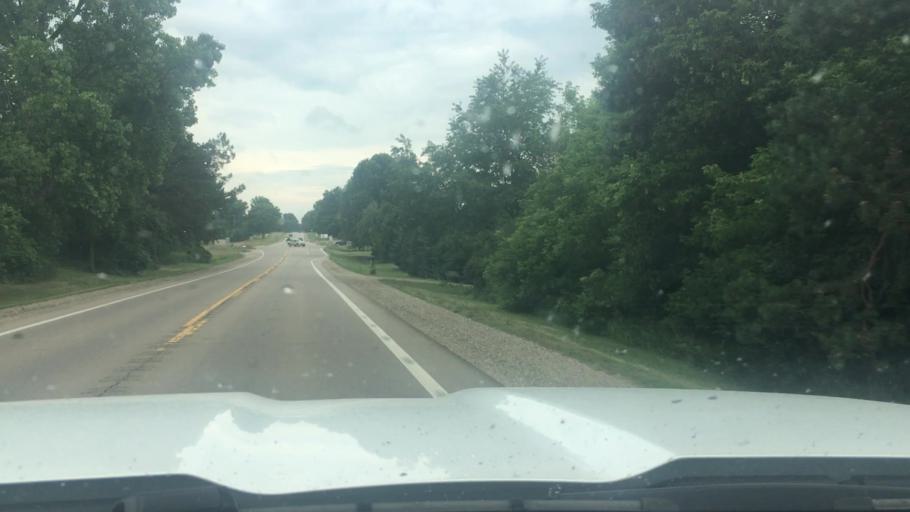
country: US
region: Michigan
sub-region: Ionia County
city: Ionia
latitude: 43.0019
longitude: -84.9925
